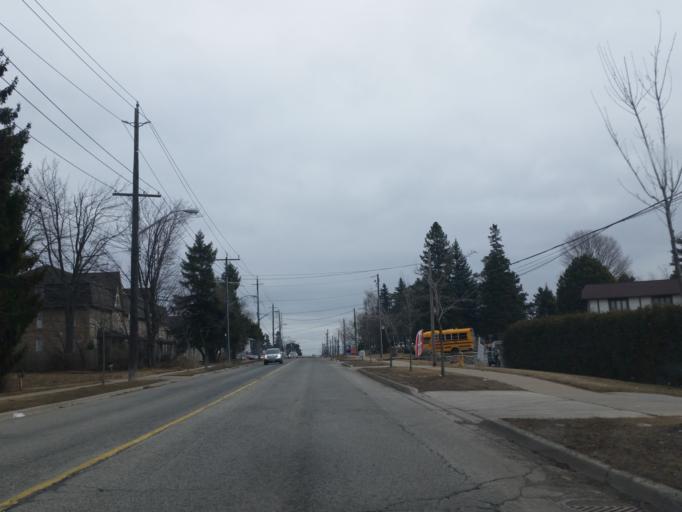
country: CA
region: Ontario
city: Scarborough
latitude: 43.7908
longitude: -79.1589
